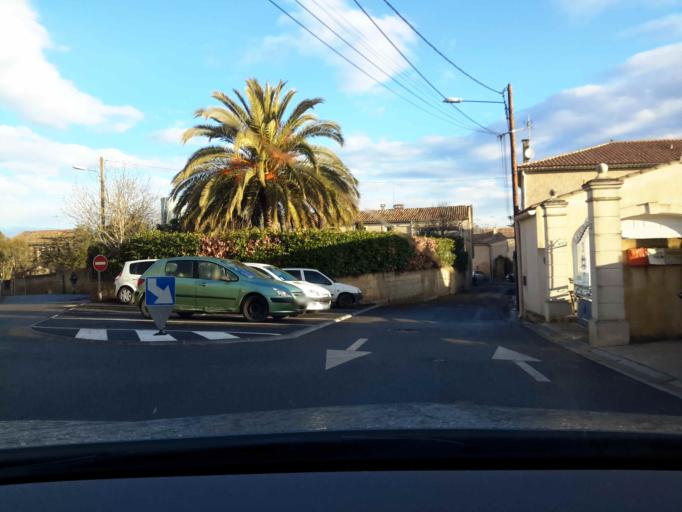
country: FR
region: Languedoc-Roussillon
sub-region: Departement du Gard
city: Beauvoisin
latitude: 43.7168
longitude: 4.3264
